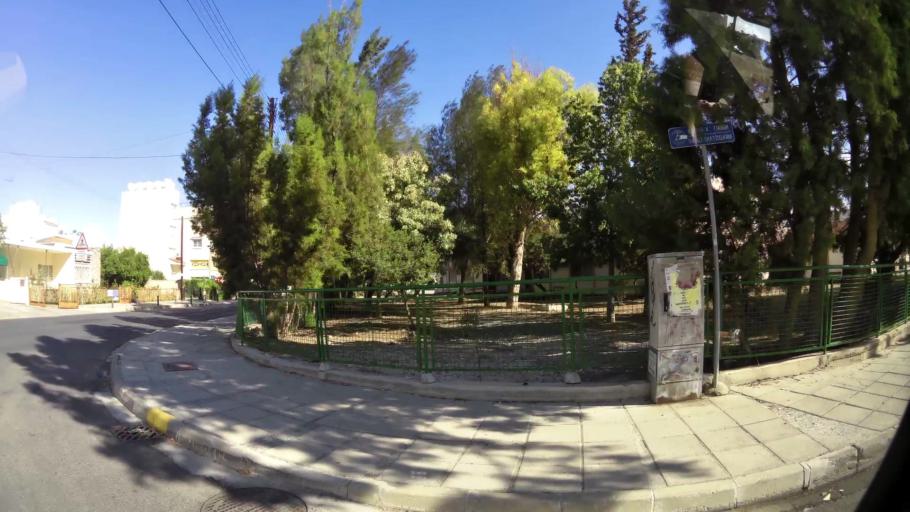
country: CY
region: Lefkosia
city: Nicosia
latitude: 35.1365
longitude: 33.3364
